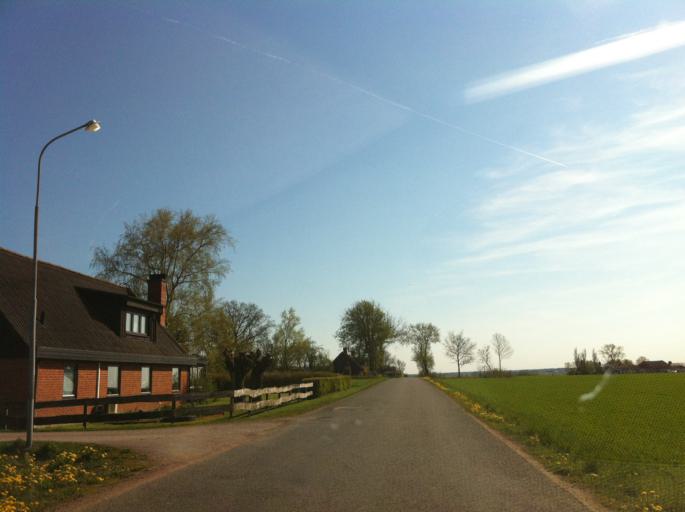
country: SE
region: Skane
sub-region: Svalovs Kommun
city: Kagerod
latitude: 55.9816
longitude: 13.0690
